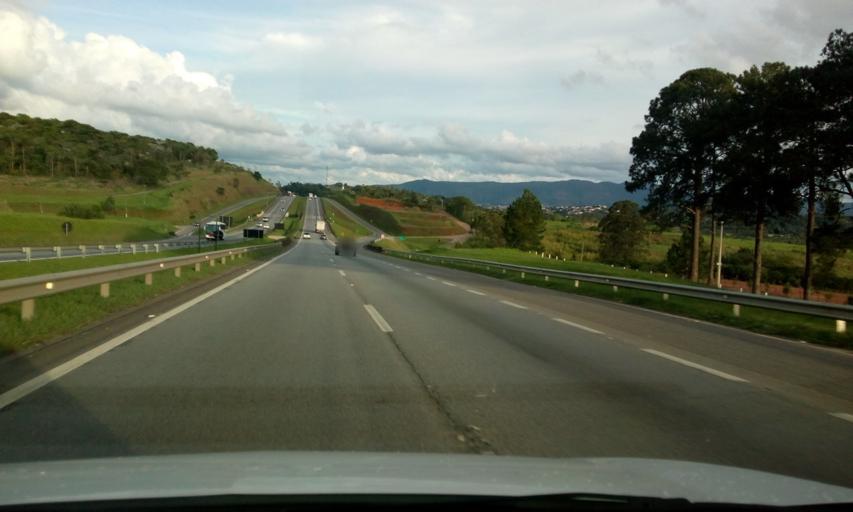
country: BR
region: Sao Paulo
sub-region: Atibaia
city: Atibaia
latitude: -23.0968
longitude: -46.6219
